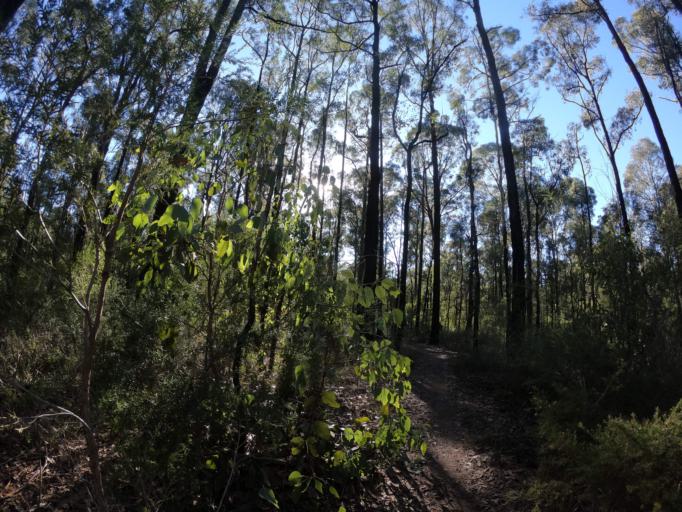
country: AU
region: New South Wales
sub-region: Hawkesbury
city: South Windsor
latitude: -33.6448
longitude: 150.7923
